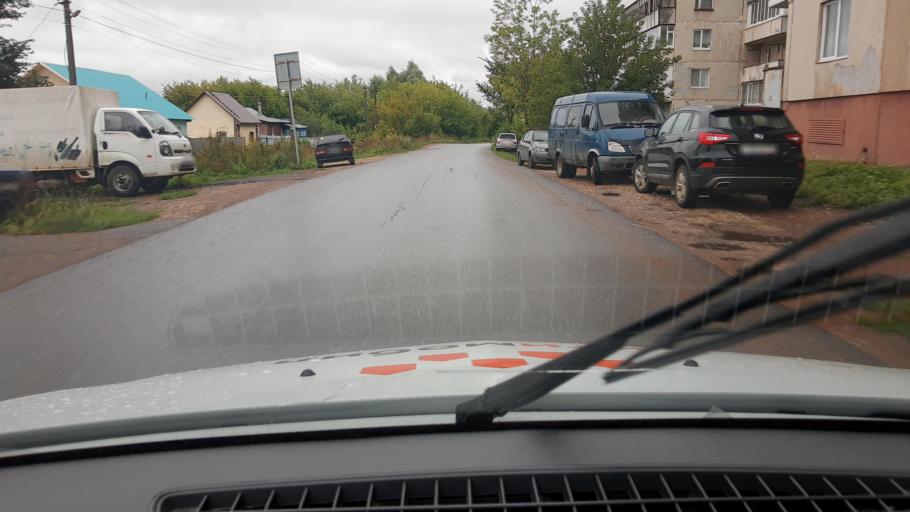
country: RU
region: Bashkortostan
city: Iglino
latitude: 54.7668
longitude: 56.2256
